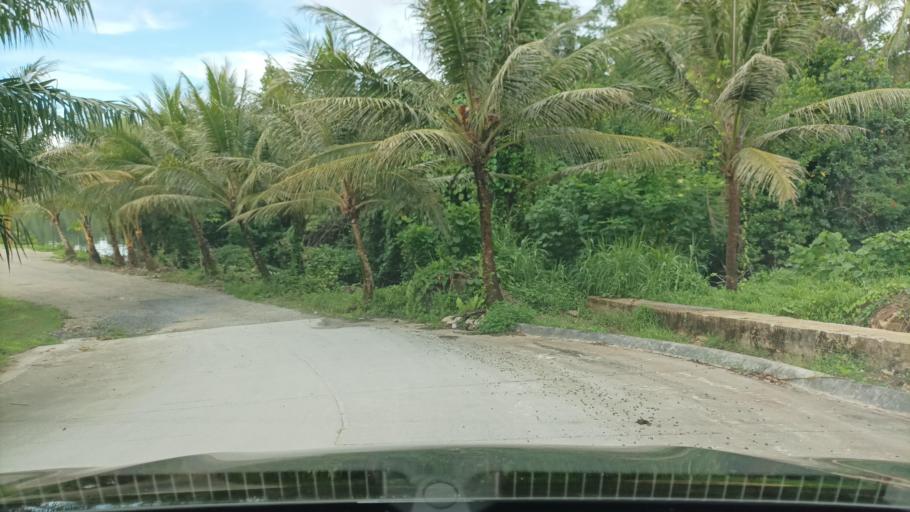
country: FM
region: Pohnpei
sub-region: Kolonia Municipality
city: Kolonia Town
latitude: 6.9572
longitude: 158.2011
